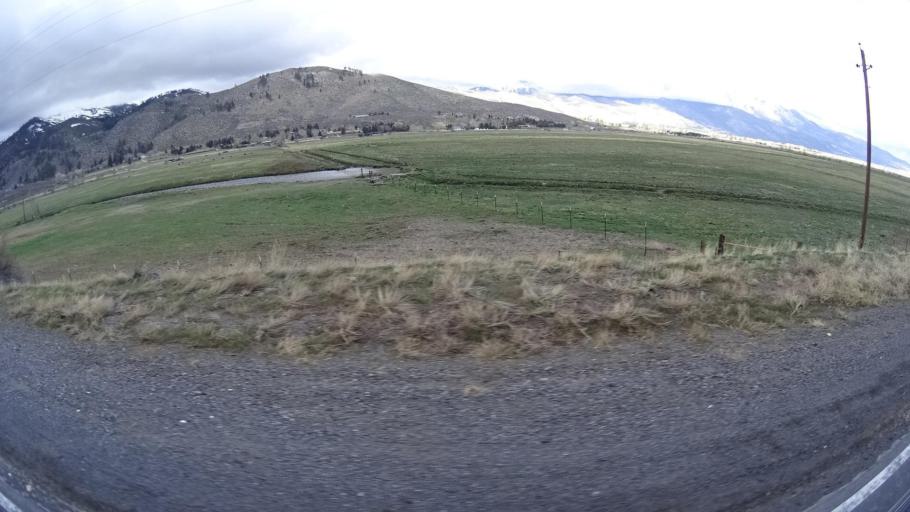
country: US
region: Nevada
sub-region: Carson City
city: Carson City
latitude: 39.2207
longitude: -119.8005
